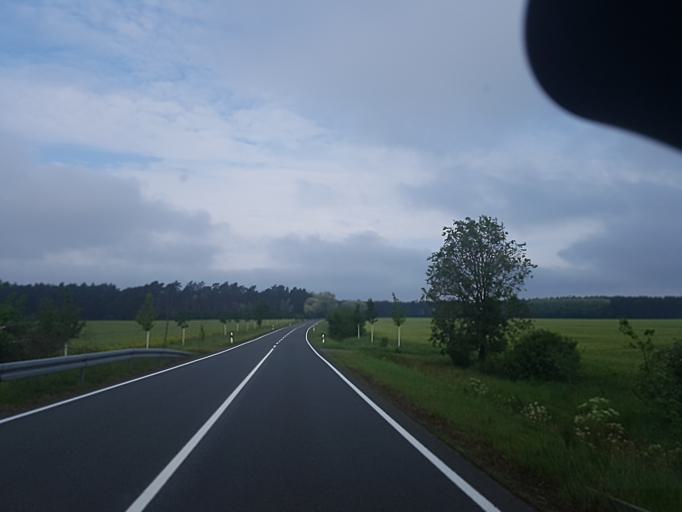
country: DE
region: Saxony-Anhalt
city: Klieken
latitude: 51.9713
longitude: 12.3199
